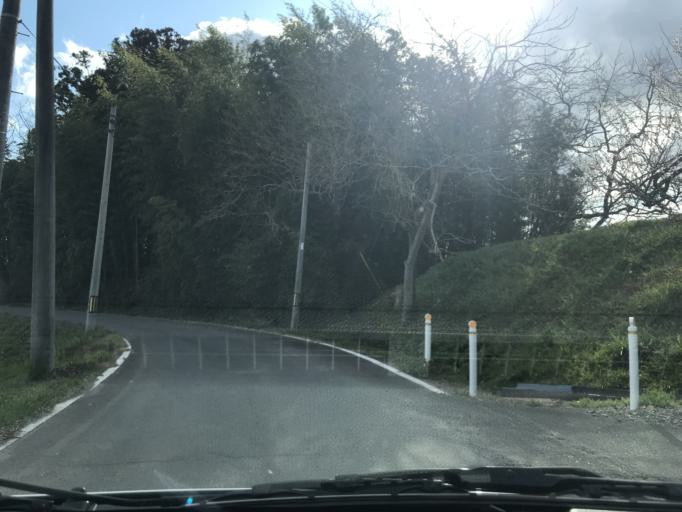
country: JP
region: Miyagi
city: Wakuya
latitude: 38.6116
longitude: 141.2299
